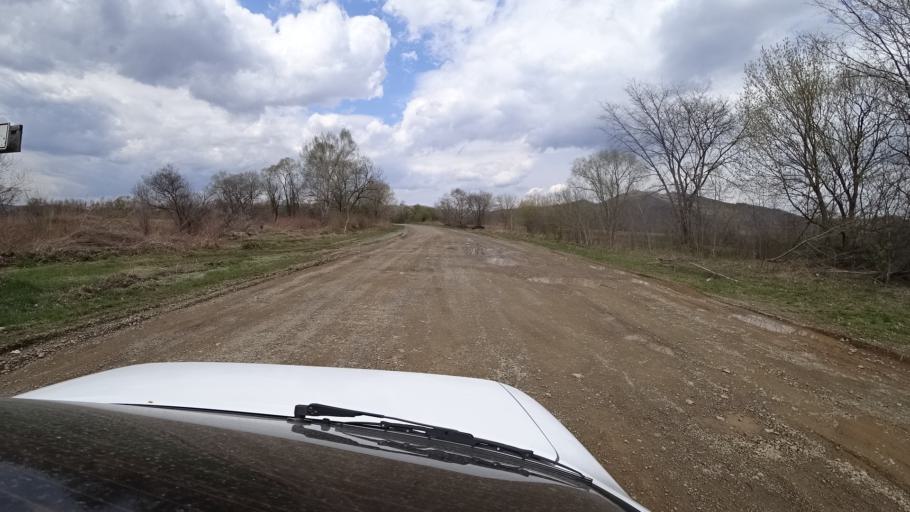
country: RU
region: Primorskiy
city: Novopokrovka
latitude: 45.6126
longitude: 134.2744
